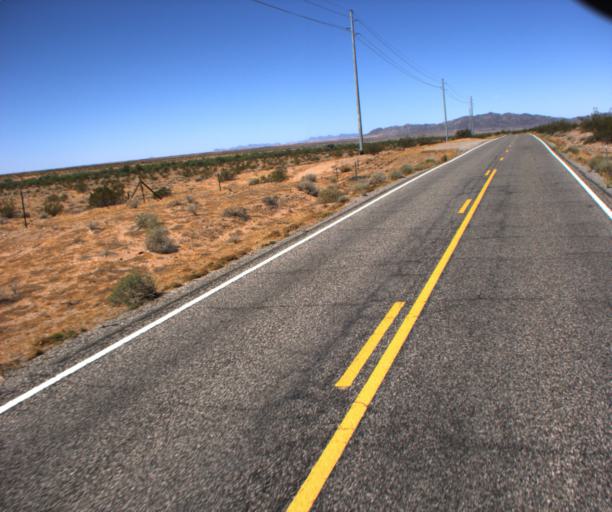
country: US
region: Arizona
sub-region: La Paz County
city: Parker
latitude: 33.9949
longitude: -114.1568
